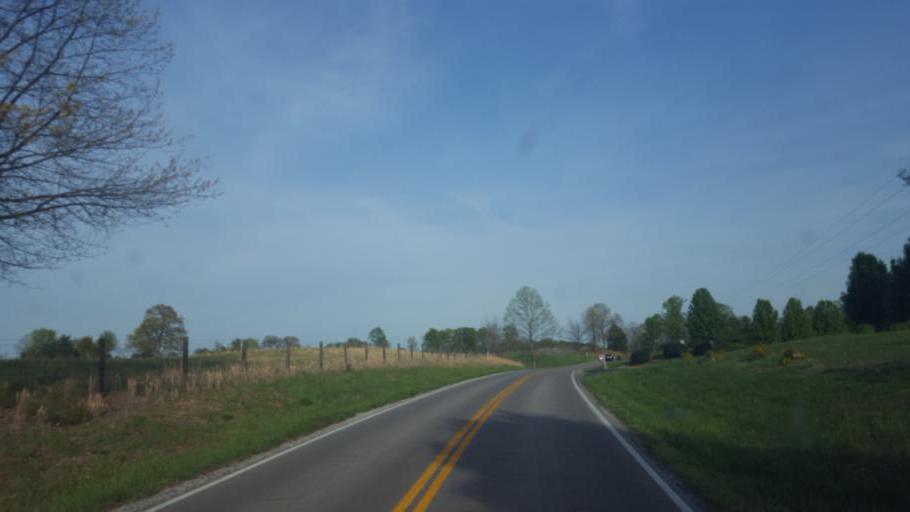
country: US
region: Kentucky
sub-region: Warren County
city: Plano
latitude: 36.9292
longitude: -86.2873
